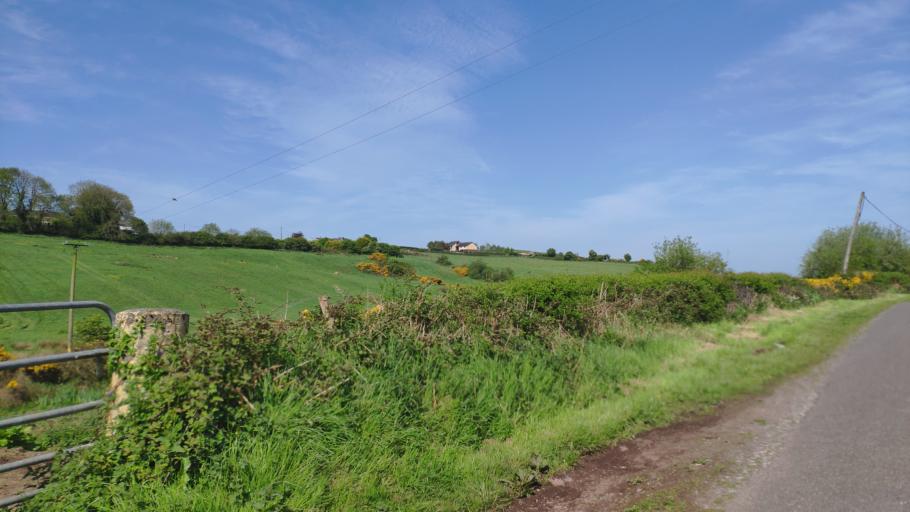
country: IE
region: Munster
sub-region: County Cork
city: Blarney
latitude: 51.9135
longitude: -8.5287
